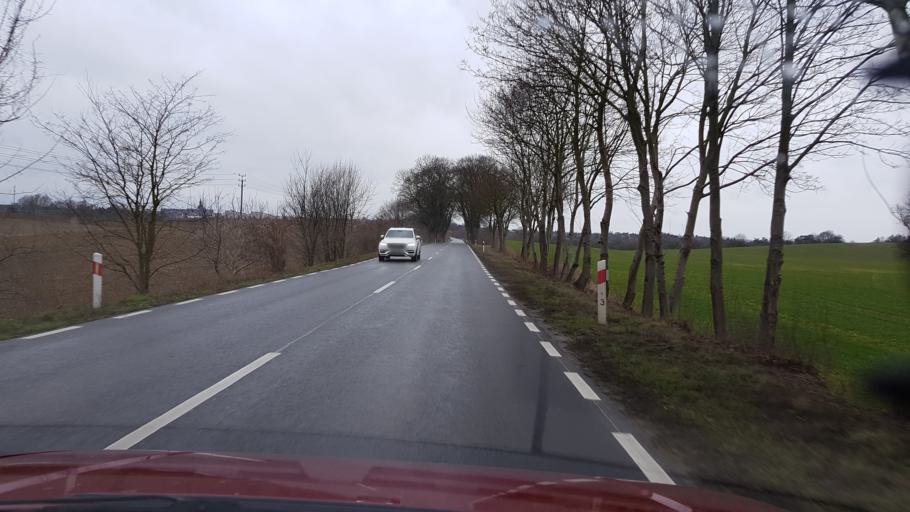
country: PL
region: West Pomeranian Voivodeship
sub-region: Powiat gryfinski
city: Gryfino
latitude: 53.2575
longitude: 14.5203
